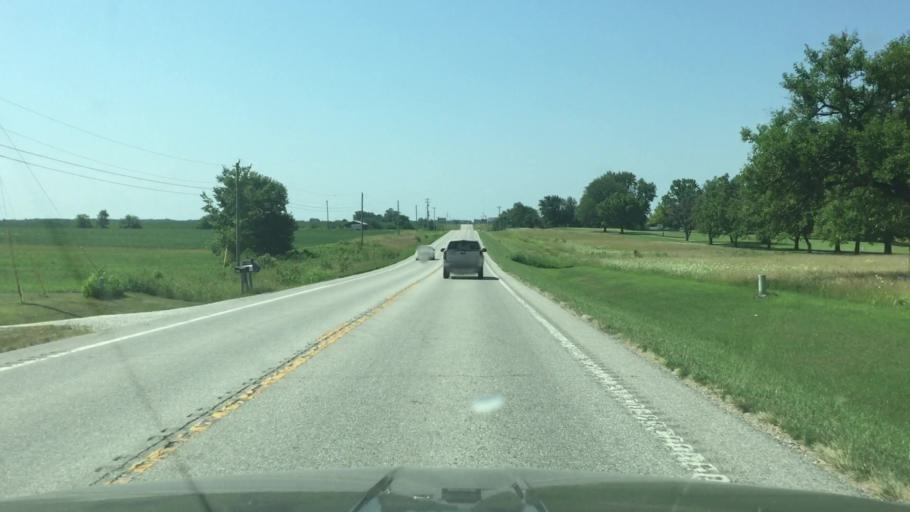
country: US
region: Missouri
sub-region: Morgan County
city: Versailles
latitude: 38.4675
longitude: -92.8089
